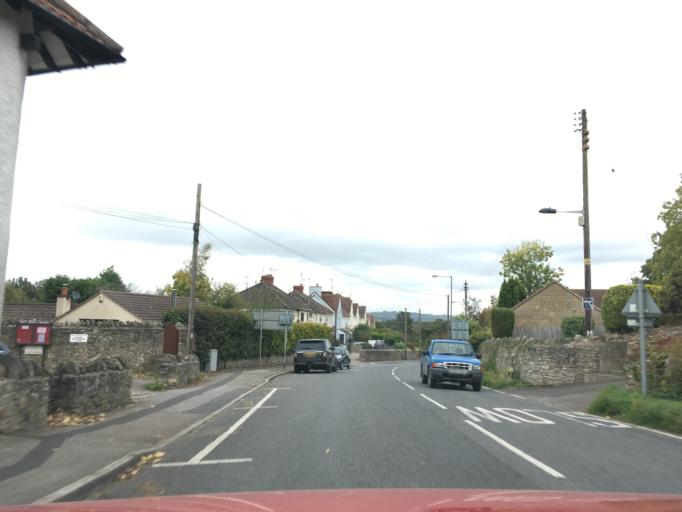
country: GB
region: England
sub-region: South Gloucestershire
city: Wickwar
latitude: 51.5971
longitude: -2.3999
